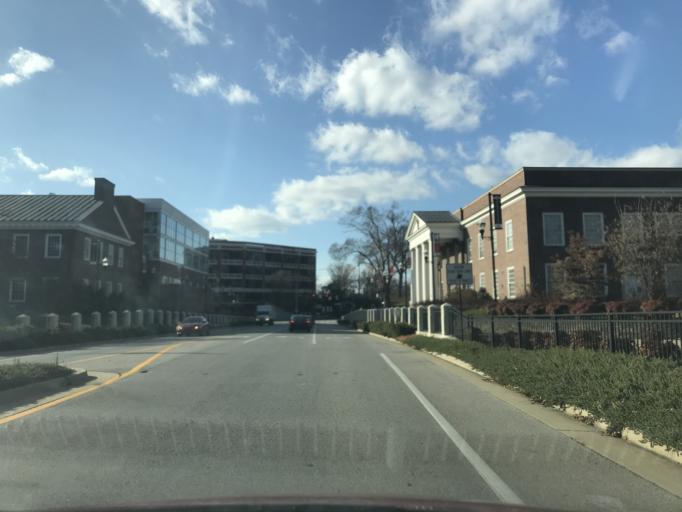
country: US
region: Kentucky
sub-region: Jefferson County
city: Audubon Park
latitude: 38.2136
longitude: -85.7607
